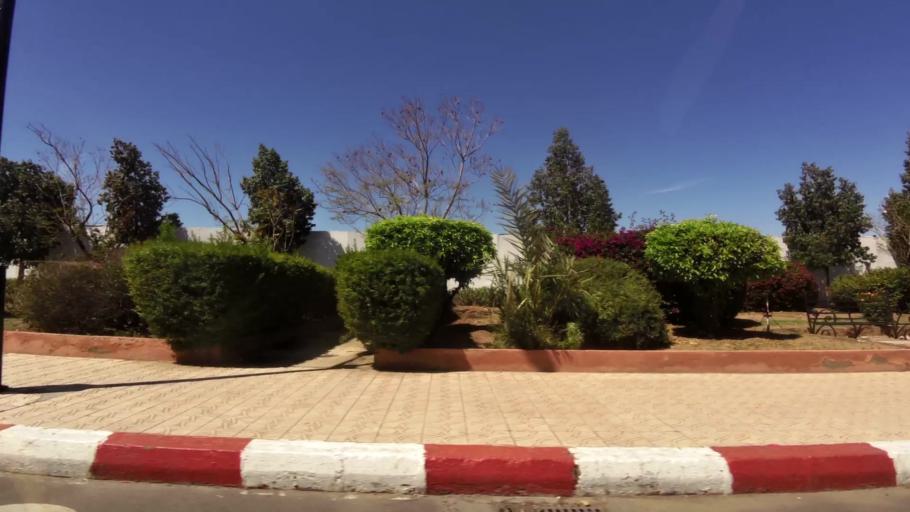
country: MA
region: Marrakech-Tensift-Al Haouz
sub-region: Marrakech
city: Marrakesh
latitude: 31.6035
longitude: -7.9883
